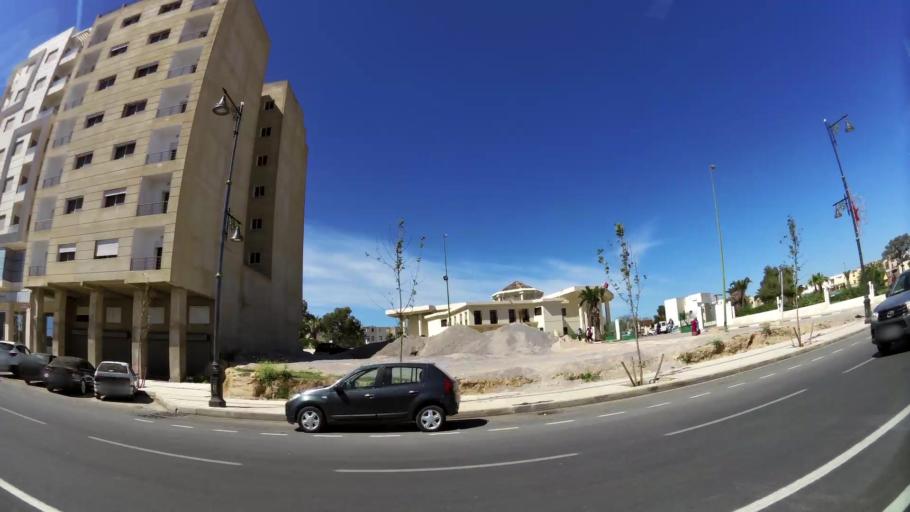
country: MA
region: Meknes-Tafilalet
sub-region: Meknes
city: Meknes
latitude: 33.8624
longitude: -5.5324
